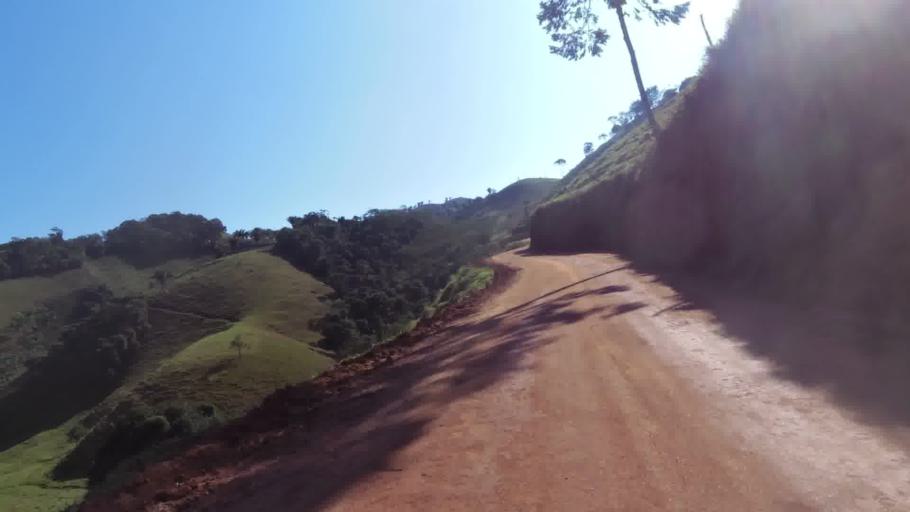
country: BR
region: Espirito Santo
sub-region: Alfredo Chaves
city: Alfredo Chaves
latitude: -20.6748
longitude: -40.7826
